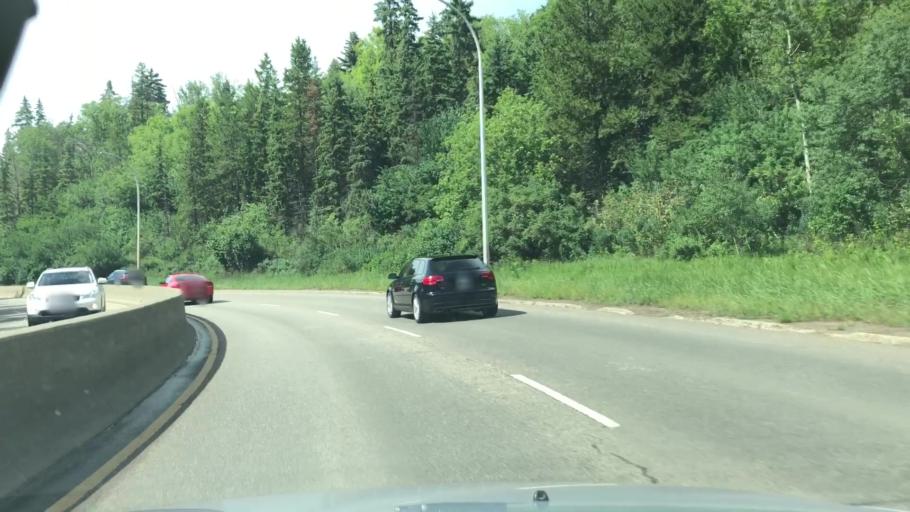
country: CA
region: Alberta
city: Edmonton
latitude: 53.5455
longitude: -113.5427
